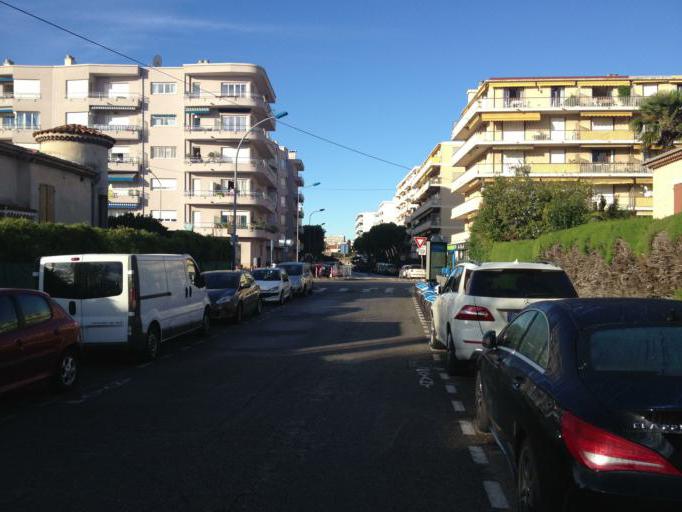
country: FR
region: Provence-Alpes-Cote d'Azur
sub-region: Departement des Alpes-Maritimes
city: Saint-Laurent-du-Var
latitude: 43.6589
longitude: 7.1702
